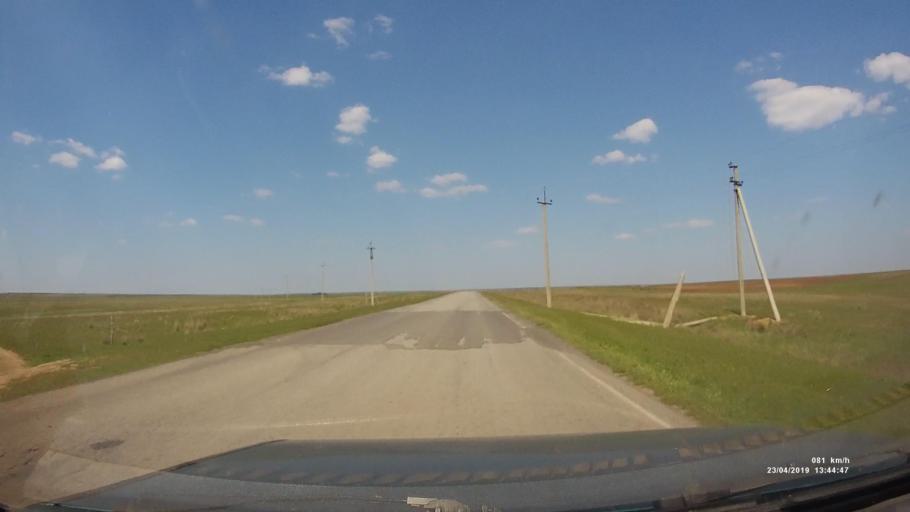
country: RU
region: Kalmykiya
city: Yashalta
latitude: 46.5849
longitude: 42.8182
